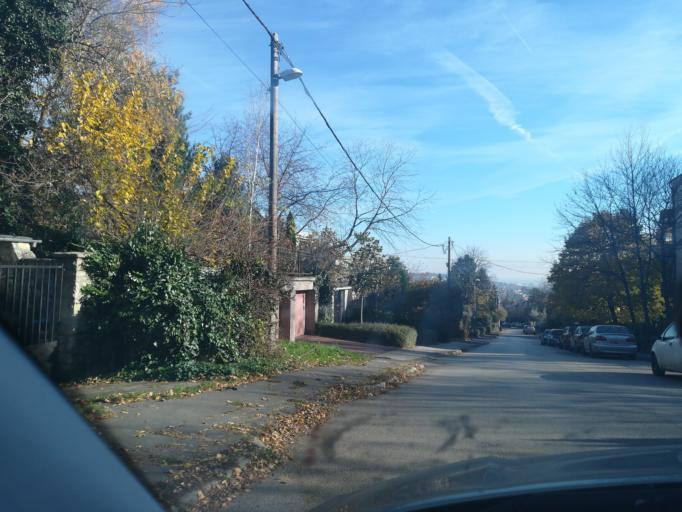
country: HU
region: Budapest
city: Budapest XII. keruelet
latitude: 47.4945
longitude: 19.0067
